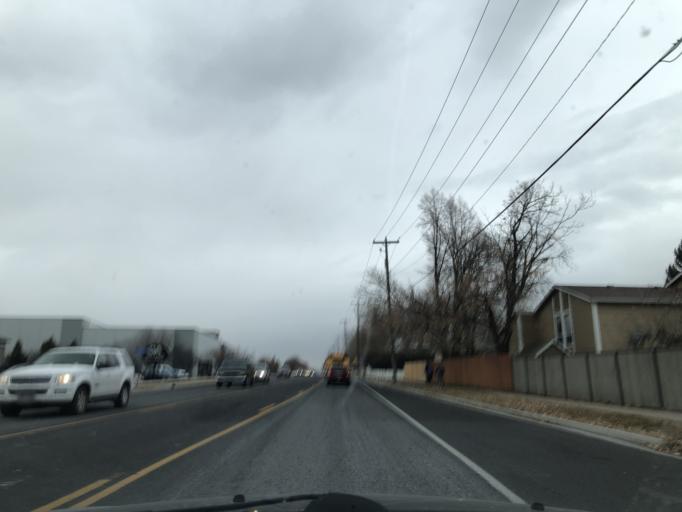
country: US
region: Utah
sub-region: Cache County
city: Logan
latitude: 41.7521
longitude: -111.8292
